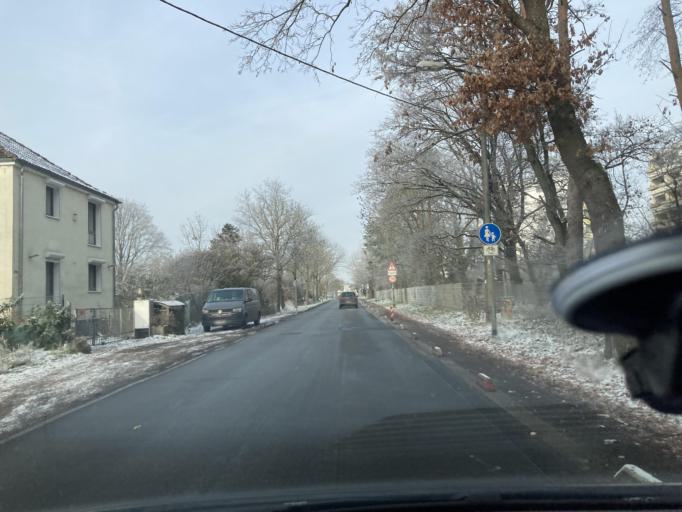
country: DE
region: Hesse
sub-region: Regierungsbezirk Darmstadt
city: Muehlheim am Main
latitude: 50.1234
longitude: 8.8073
